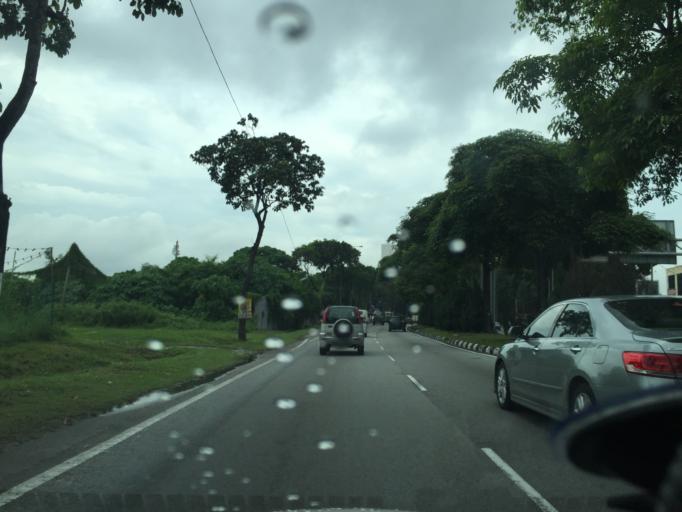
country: MY
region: Selangor
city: Klang
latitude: 3.0012
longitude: 101.4427
